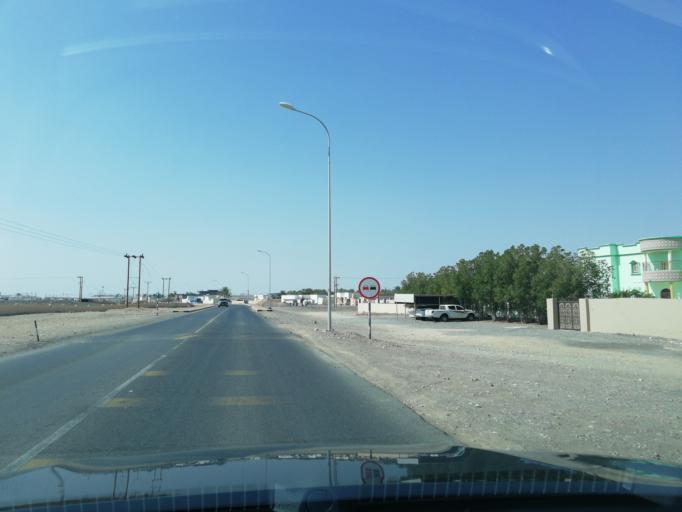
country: OM
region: Muhafazat ad Dakhiliyah
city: Adam
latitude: 22.3044
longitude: 58.0720
